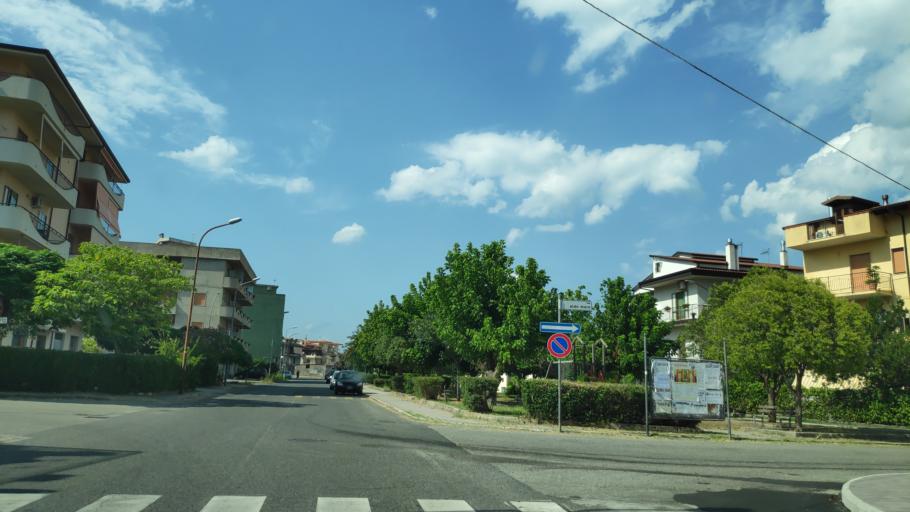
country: IT
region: Calabria
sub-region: Provincia di Catanzaro
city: Marina di Davoli
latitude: 38.6660
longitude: 16.5421
